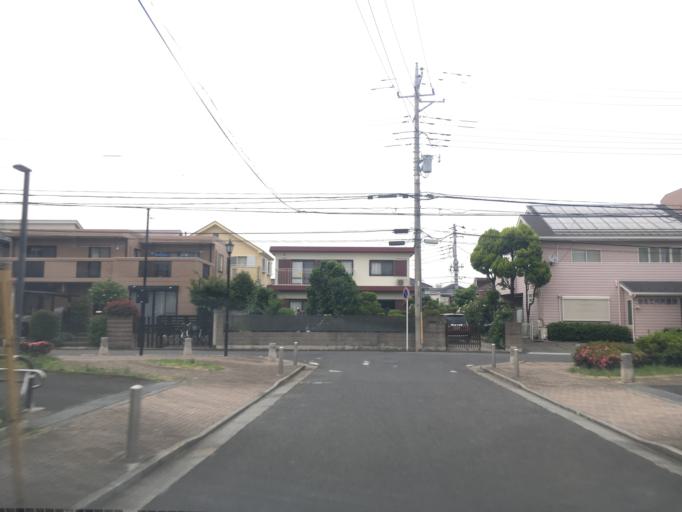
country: JP
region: Saitama
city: Tokorozawa
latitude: 35.8074
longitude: 139.4471
